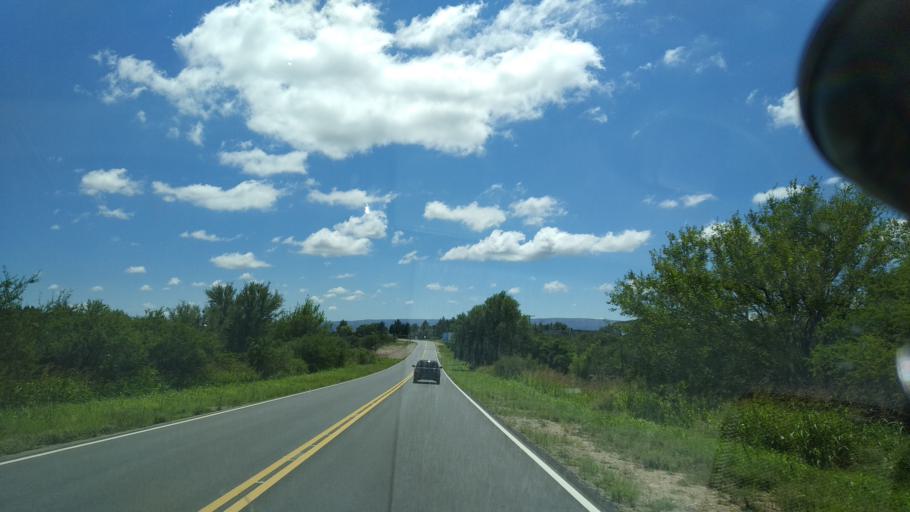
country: AR
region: Cordoba
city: Salsacate
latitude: -31.3490
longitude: -65.0840
